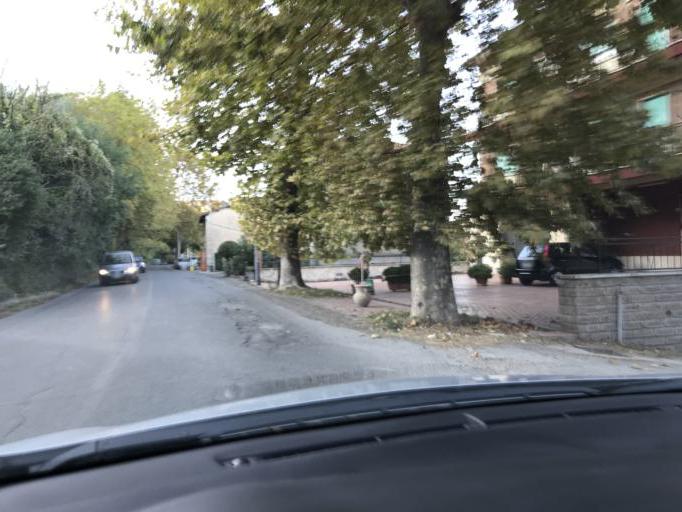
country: IT
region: Latium
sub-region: Provincia di Viterbo
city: Orte
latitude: 42.4534
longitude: 12.3880
